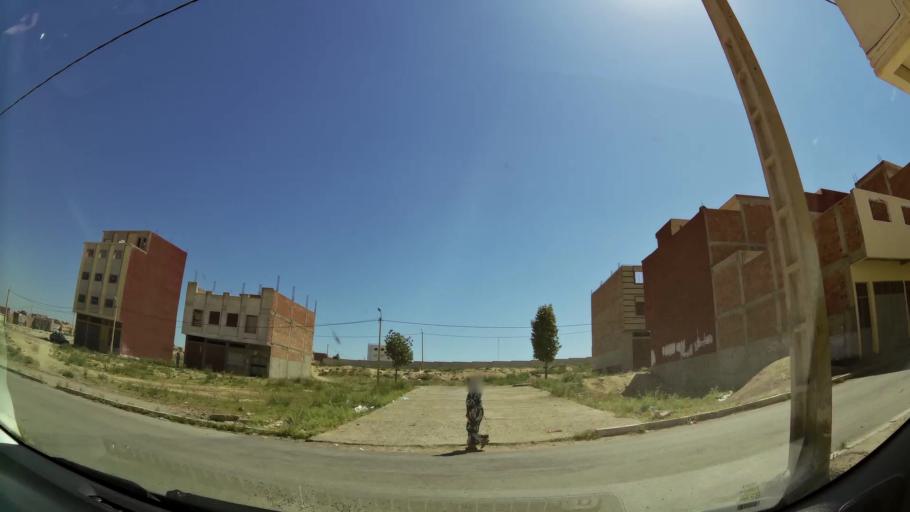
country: MA
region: Oriental
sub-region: Oujda-Angad
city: Oujda
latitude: 34.6551
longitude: -1.8730
